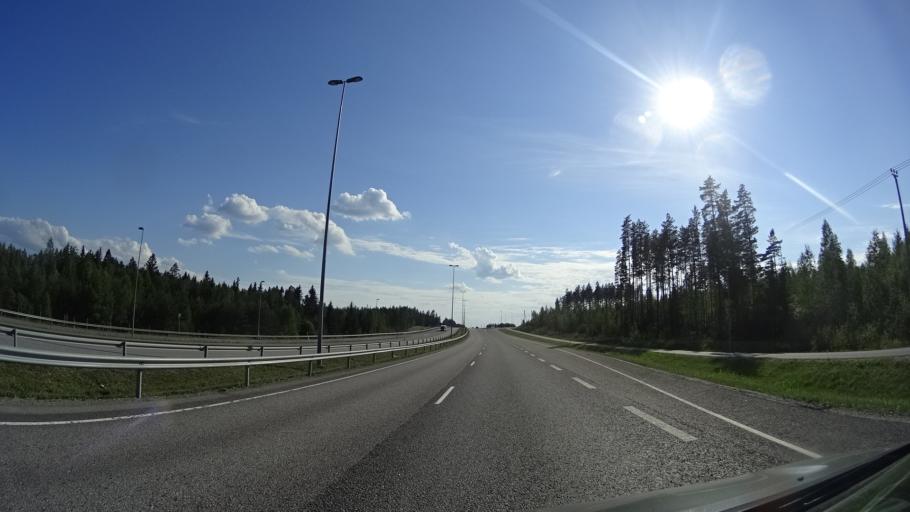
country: FI
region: South Karelia
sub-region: Imatra
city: Imatra
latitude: 61.1560
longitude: 28.6346
